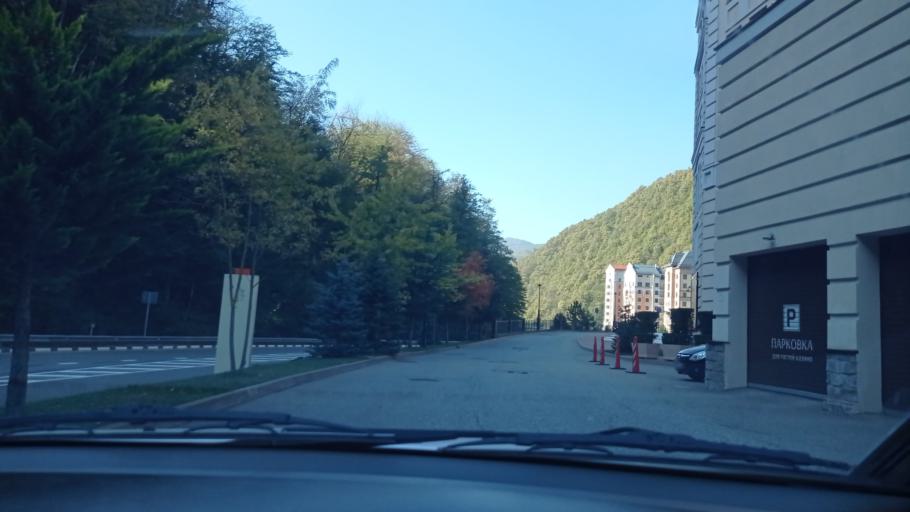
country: RU
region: Krasnodarskiy
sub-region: Sochi City
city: Krasnaya Polyana
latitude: 43.6736
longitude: 40.2886
